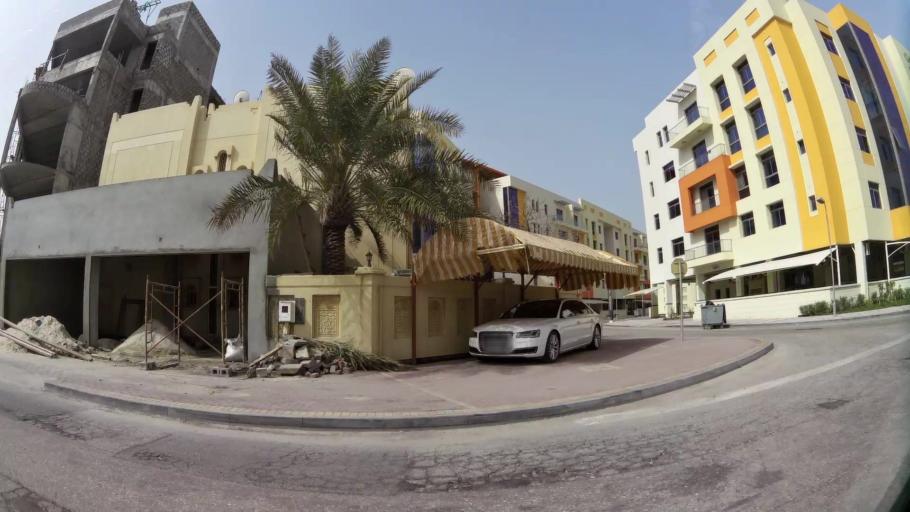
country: BH
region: Manama
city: Jidd Hafs
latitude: 26.2343
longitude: 50.5319
